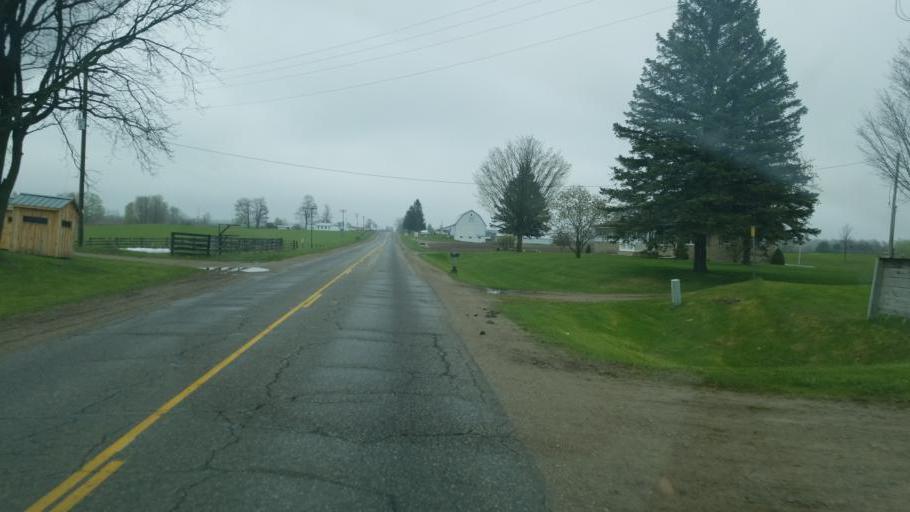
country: US
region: Michigan
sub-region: Mecosta County
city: Canadian Lakes
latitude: 43.5424
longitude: -85.3684
